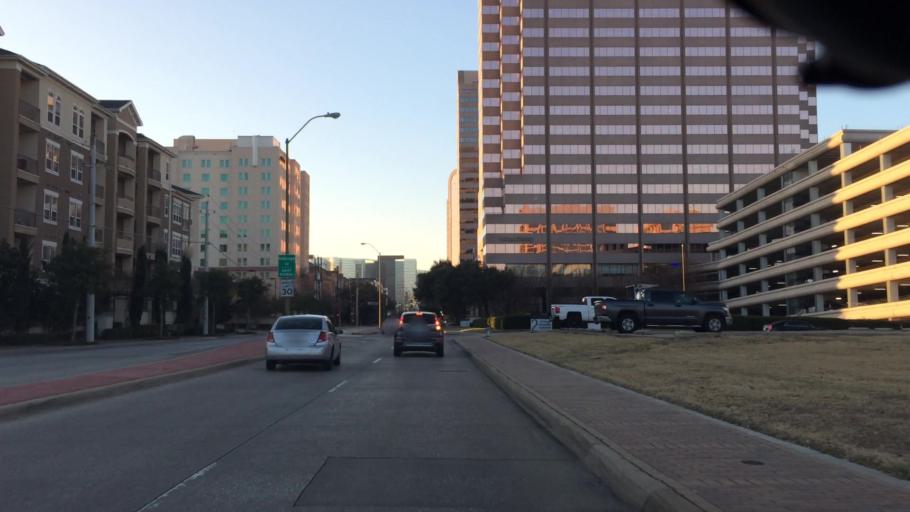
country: US
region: Texas
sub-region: Dallas County
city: Addison
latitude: 32.9325
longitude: -96.8181
